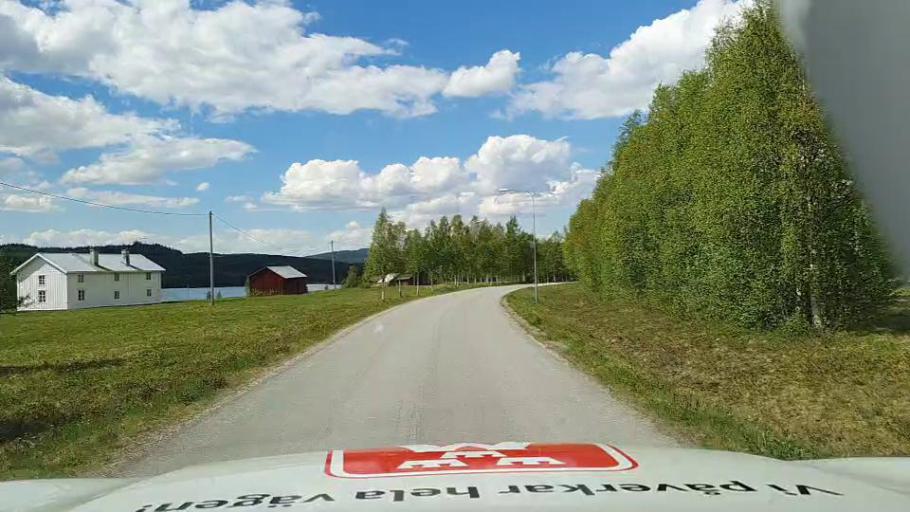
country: NO
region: Nord-Trondelag
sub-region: Lierne
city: Sandvika
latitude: 64.1223
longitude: 14.1347
